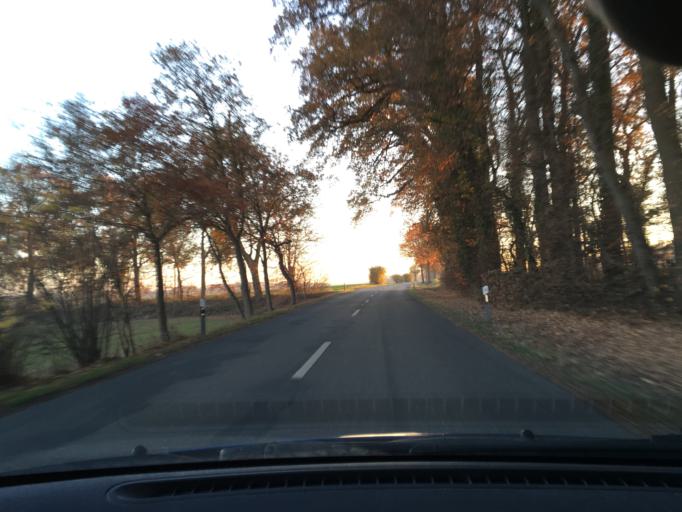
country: DE
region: Lower Saxony
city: Natendorf
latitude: 53.0755
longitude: 10.4626
